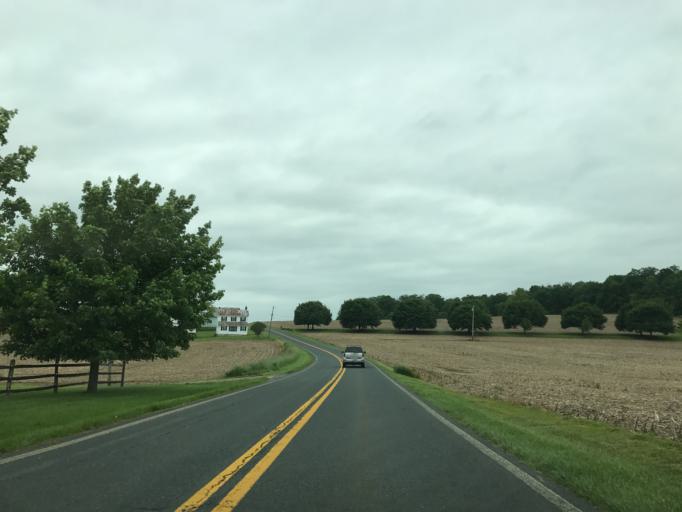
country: US
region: Maryland
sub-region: Carroll County
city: Hampstead
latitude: 39.5973
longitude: -76.8911
